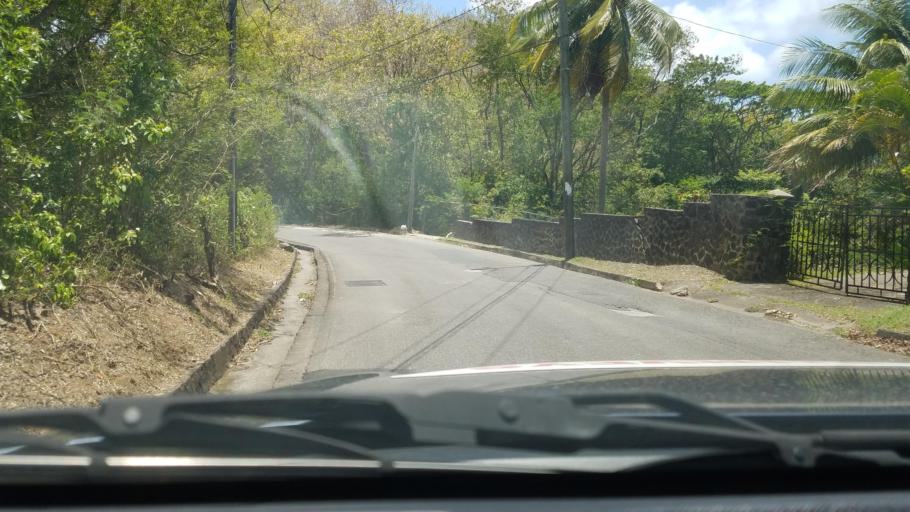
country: LC
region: Gros-Islet
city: Gros Islet
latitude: 14.0623
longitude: -60.9531
